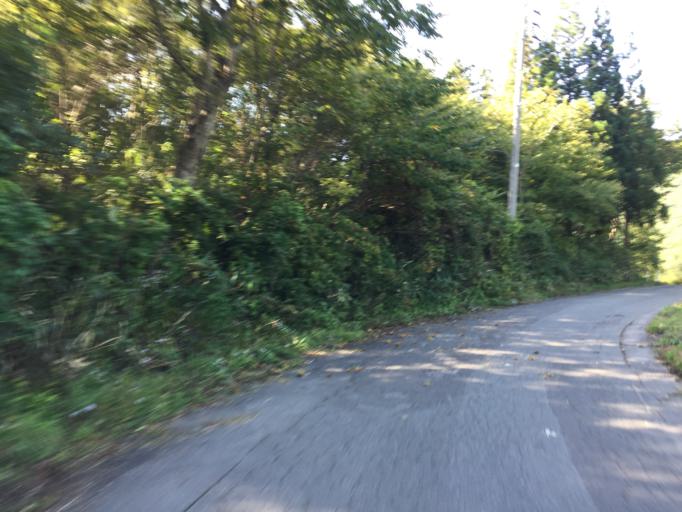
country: JP
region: Yamagata
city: Yonezawa
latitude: 37.8425
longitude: 140.1943
